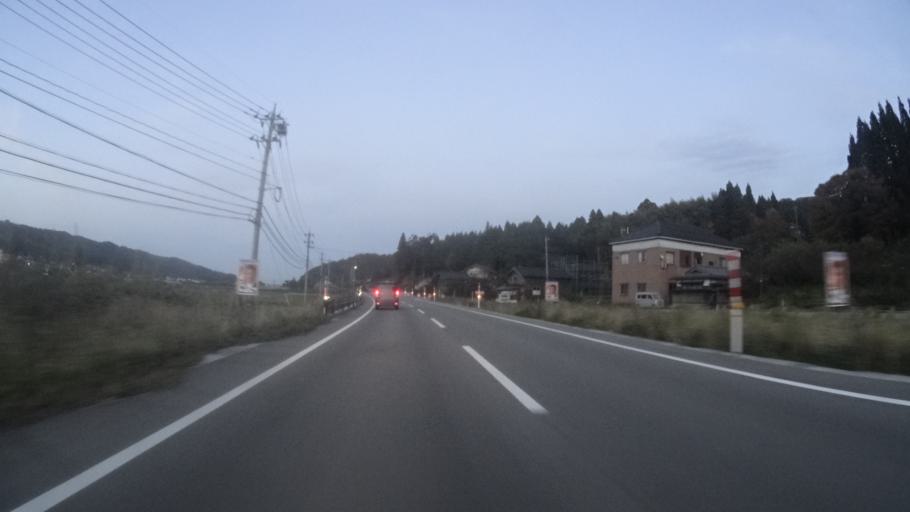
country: JP
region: Ishikawa
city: Nanao
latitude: 37.3683
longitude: 136.8726
